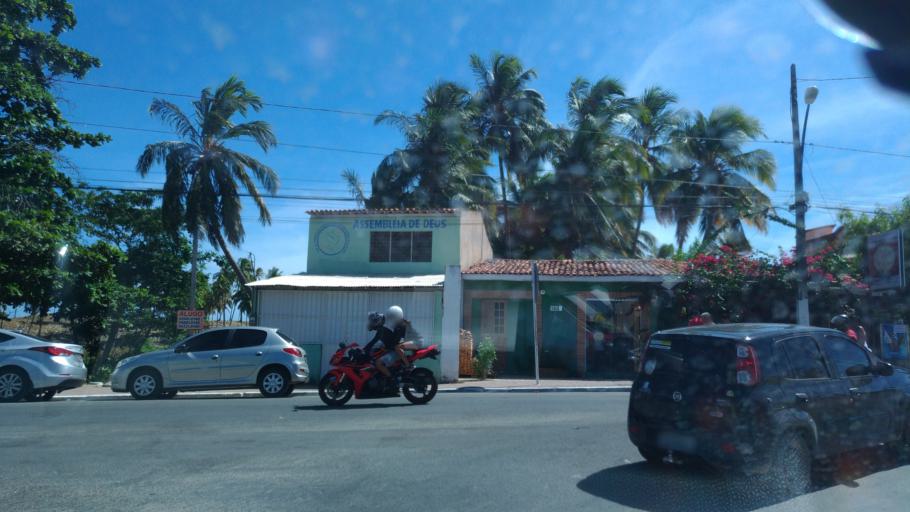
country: BR
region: Alagoas
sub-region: Marechal Deodoro
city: Marechal Deodoro
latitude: -9.7696
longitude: -35.8443
